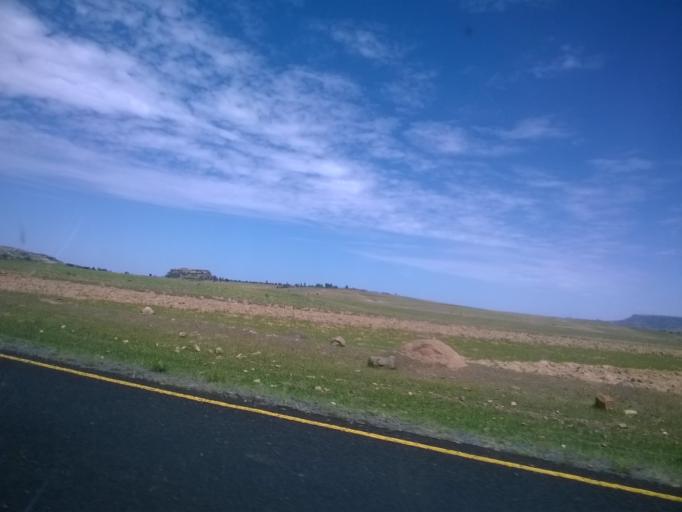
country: LS
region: Berea
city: Teyateyaneng
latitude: -29.0915
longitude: 27.8572
